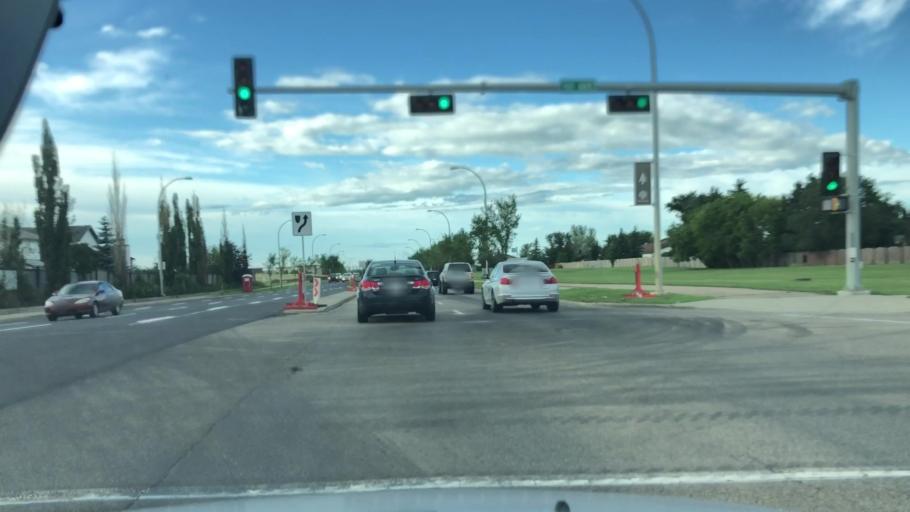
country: CA
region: Alberta
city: St. Albert
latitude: 53.6236
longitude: -113.5411
